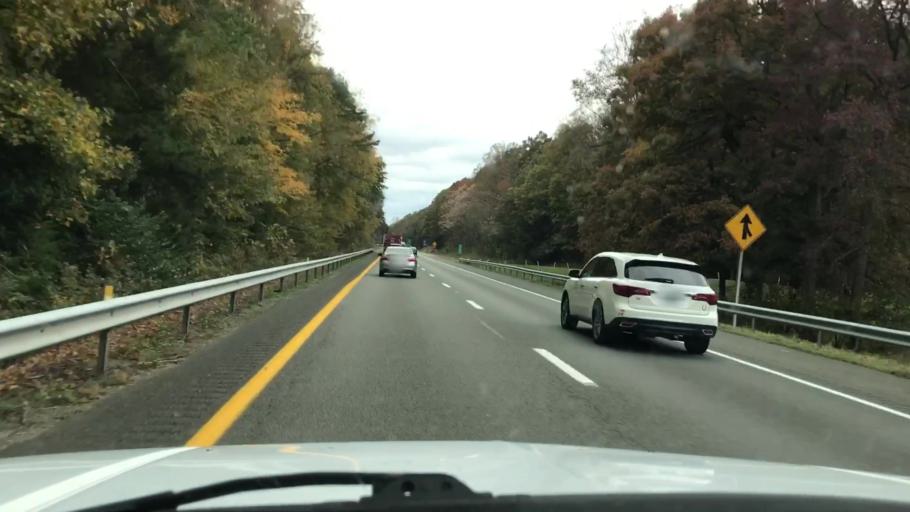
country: US
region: Virginia
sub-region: Goochland County
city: Goochland
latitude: 37.7056
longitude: -77.7648
